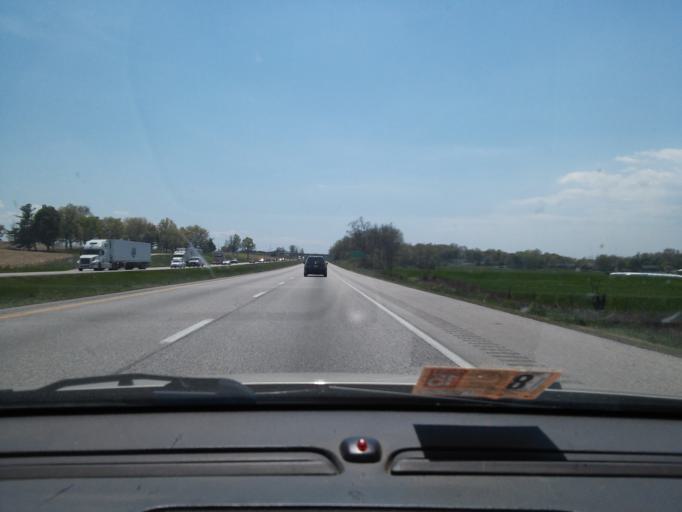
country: US
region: Pennsylvania
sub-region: Franklin County
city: Greencastle
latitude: 39.8229
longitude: -77.7008
